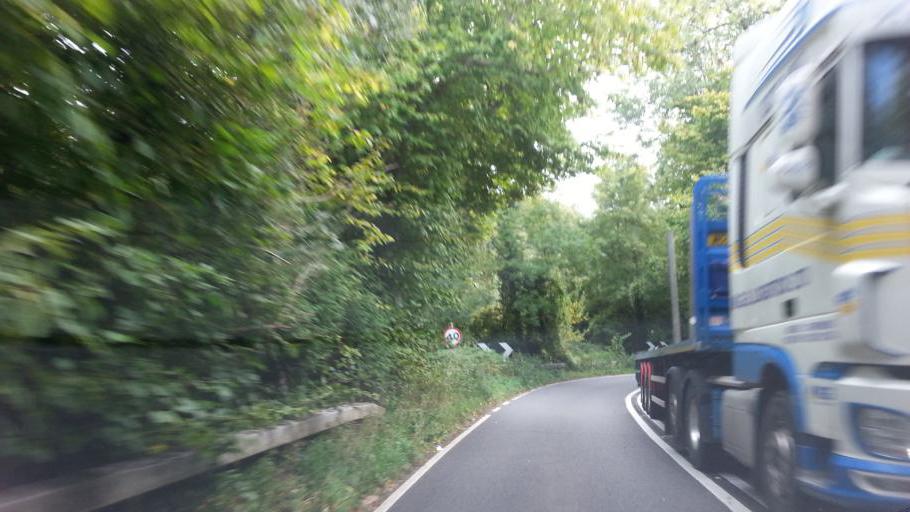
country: GB
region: England
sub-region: Gloucestershire
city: Mitcheldean
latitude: 51.8775
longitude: -2.4315
